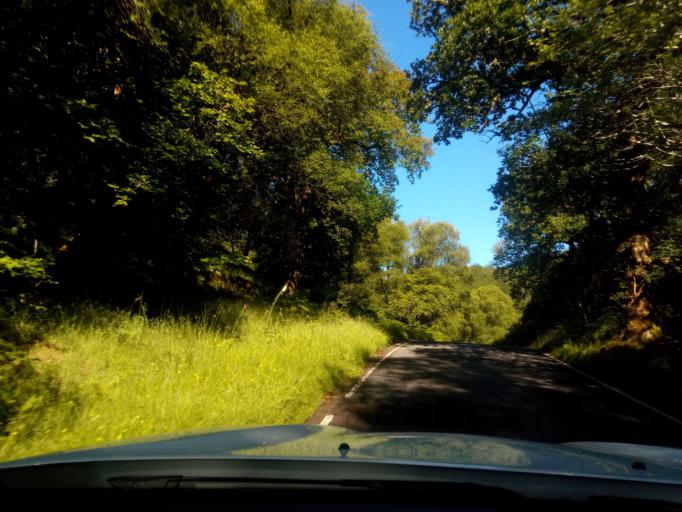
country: GB
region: Scotland
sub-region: Argyll and Bute
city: Isle Of Mull
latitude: 56.6922
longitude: -5.6690
